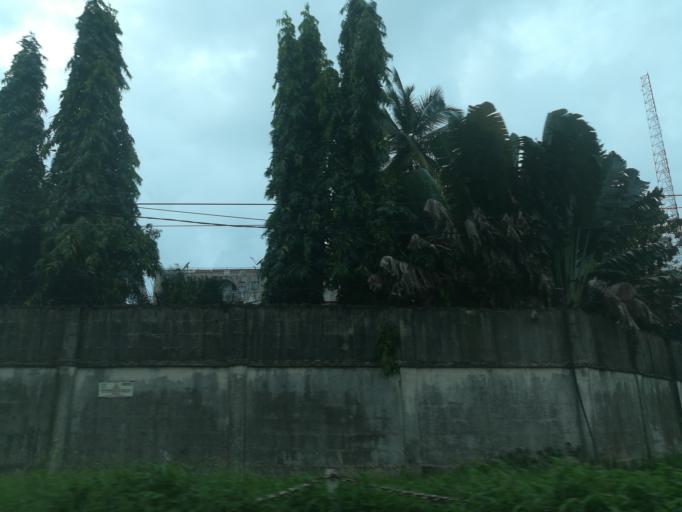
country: NG
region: Lagos
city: Ikoyi
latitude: 6.4239
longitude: 3.4191
